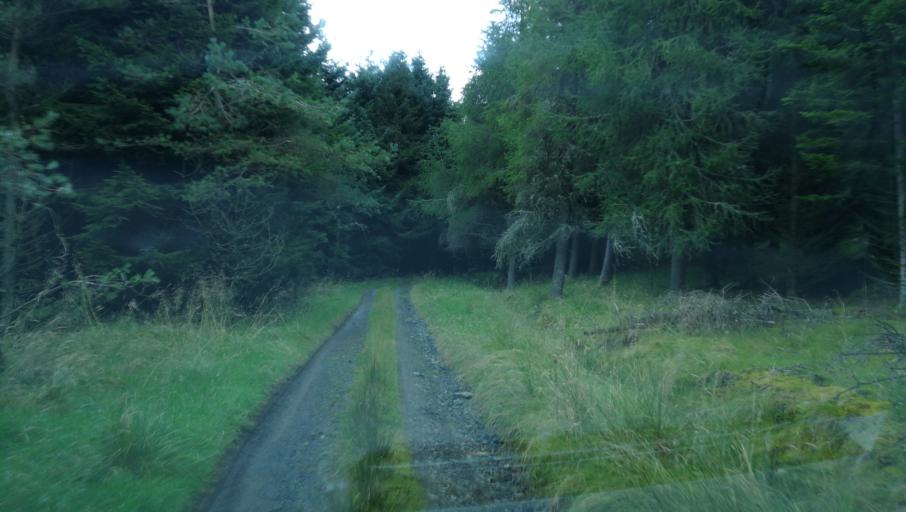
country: GB
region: Scotland
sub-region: Perth and Kinross
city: Blairgowrie
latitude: 56.6687
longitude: -3.3474
